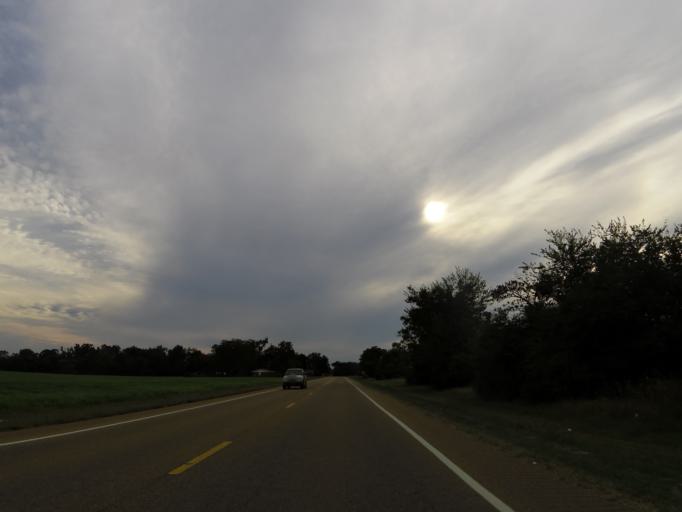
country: US
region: Alabama
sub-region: Monroe County
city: Frisco City
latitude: 31.4216
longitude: -87.4175
